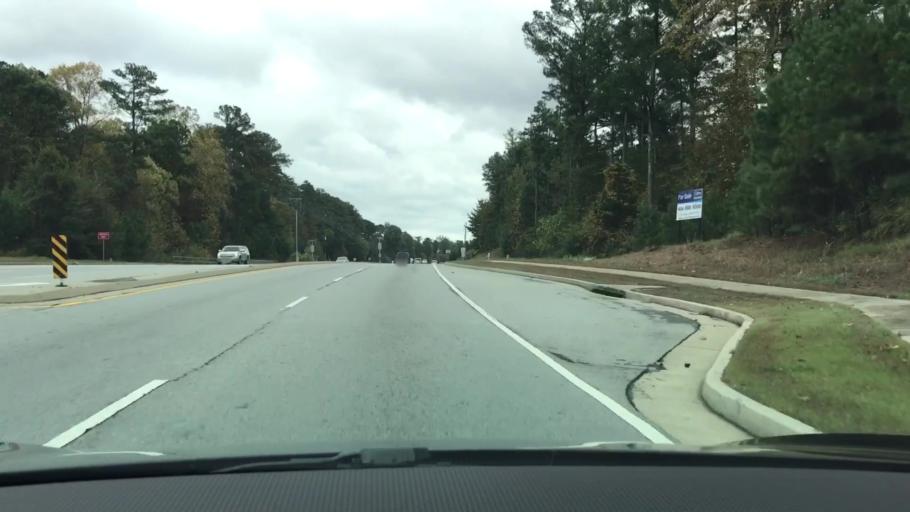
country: US
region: Georgia
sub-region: Gwinnett County
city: Suwanee
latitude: 34.0303
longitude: -84.0622
